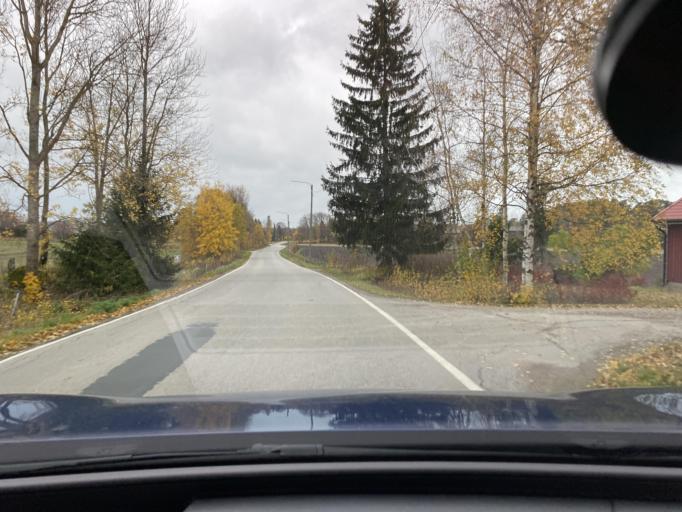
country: FI
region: Varsinais-Suomi
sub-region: Vakka-Suomi
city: Laitila
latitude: 60.9217
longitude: 21.5999
